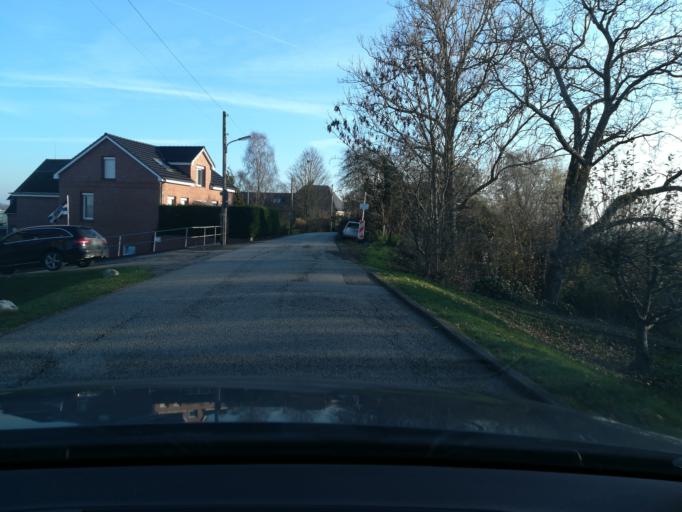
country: DE
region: Lower Saxony
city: Stelle
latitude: 53.4484
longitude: 10.1038
